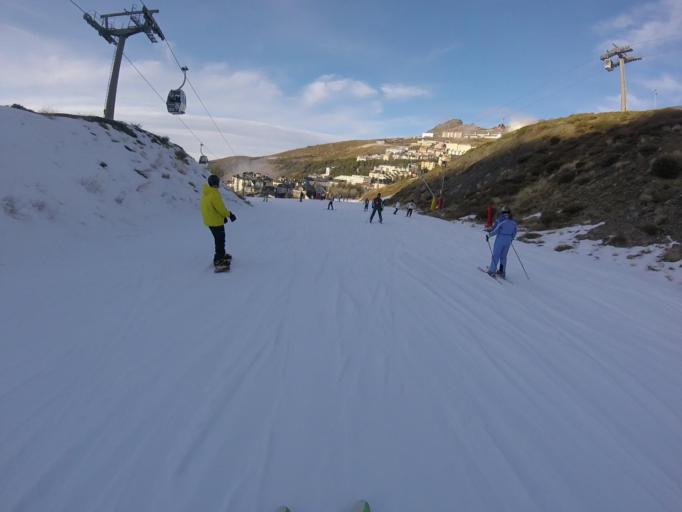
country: ES
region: Andalusia
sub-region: Provincia de Granada
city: Guejar-Sierra
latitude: 37.0907
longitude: -3.3984
